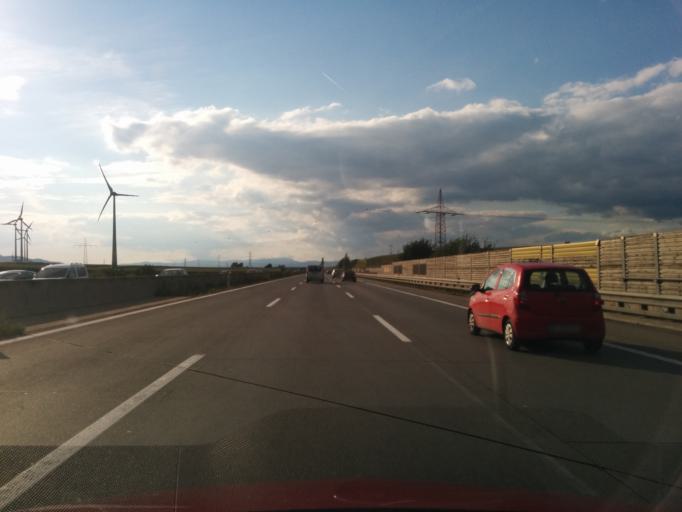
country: AT
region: Lower Austria
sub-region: Politischer Bezirk Sankt Polten
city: Haunoldstein
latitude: 48.1772
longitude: 15.4610
